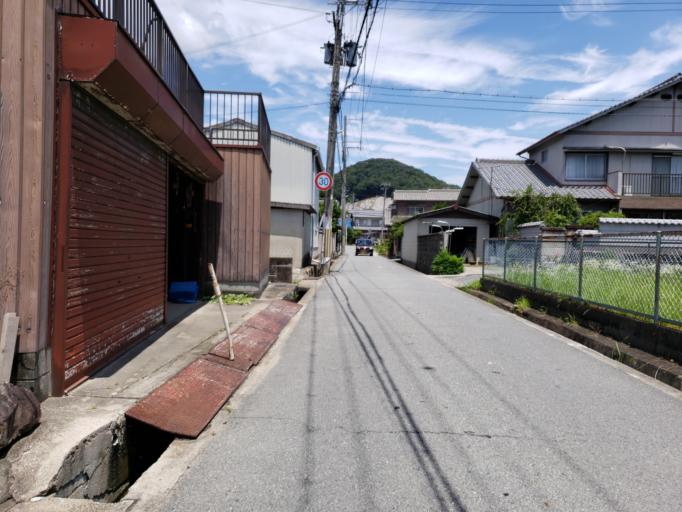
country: JP
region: Hyogo
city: Kakogawacho-honmachi
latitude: 34.8216
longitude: 134.8116
